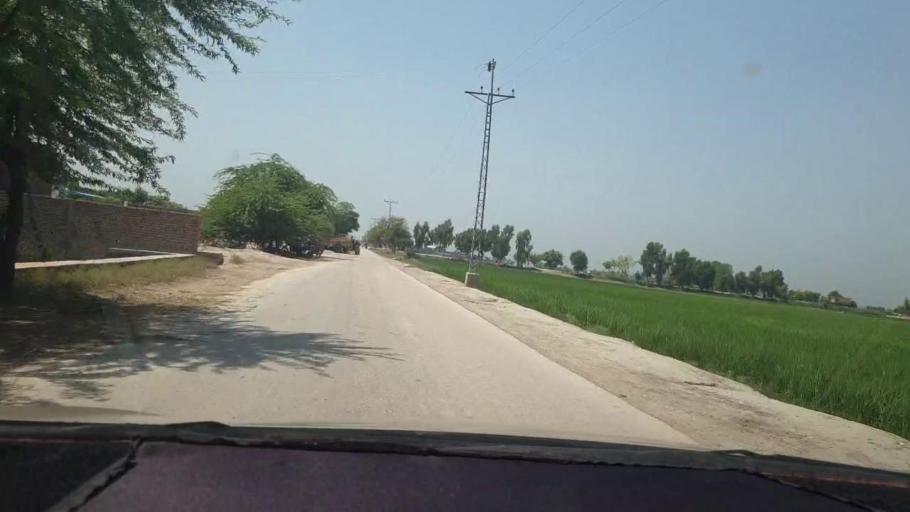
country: PK
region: Sindh
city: Kambar
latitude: 27.5974
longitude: 68.0226
